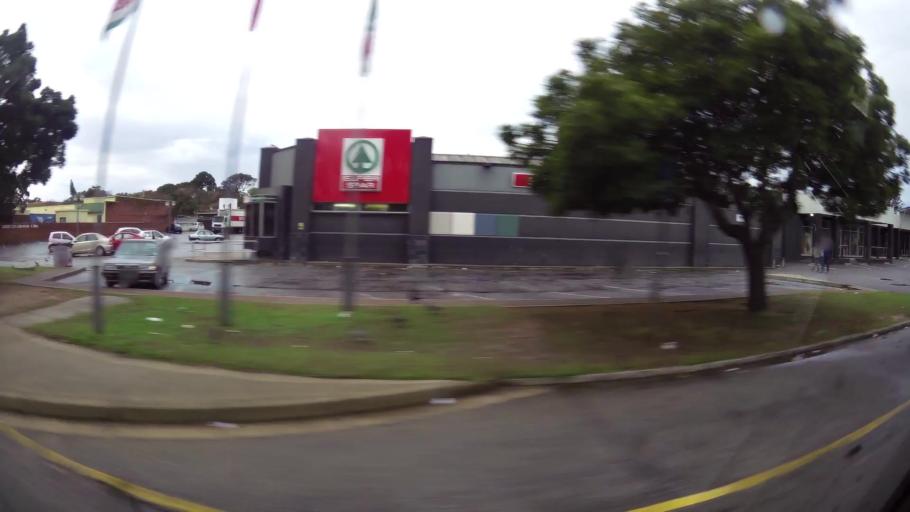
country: ZA
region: Eastern Cape
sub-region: Nelson Mandela Bay Metropolitan Municipality
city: Port Elizabeth
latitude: -33.9791
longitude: 25.5839
